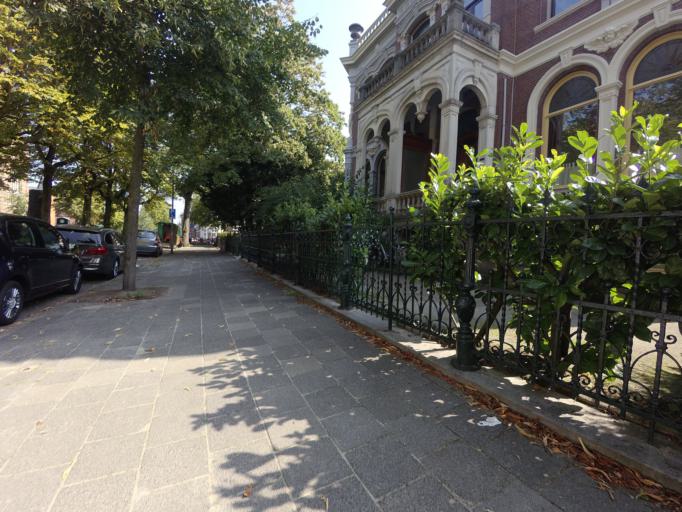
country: NL
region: Groningen
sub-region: Gemeente Groningen
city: Groningen
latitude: 53.2140
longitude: 6.5722
